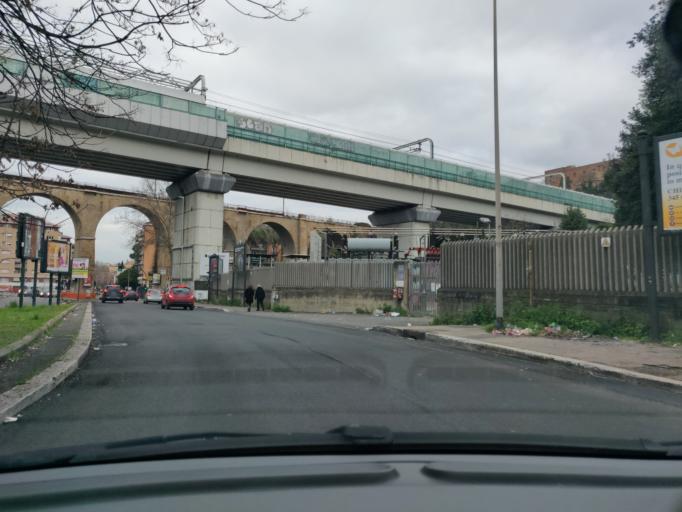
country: VA
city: Vatican City
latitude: 41.9023
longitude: 12.4420
